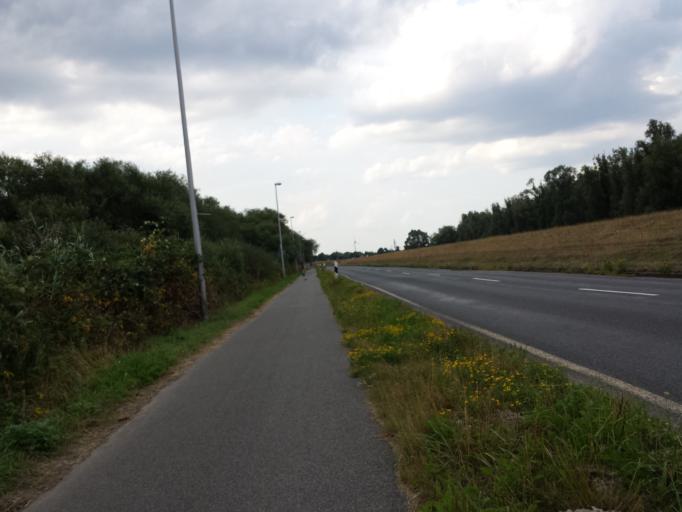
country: DE
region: Lower Saxony
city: Stuhr
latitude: 53.1028
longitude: 8.7243
